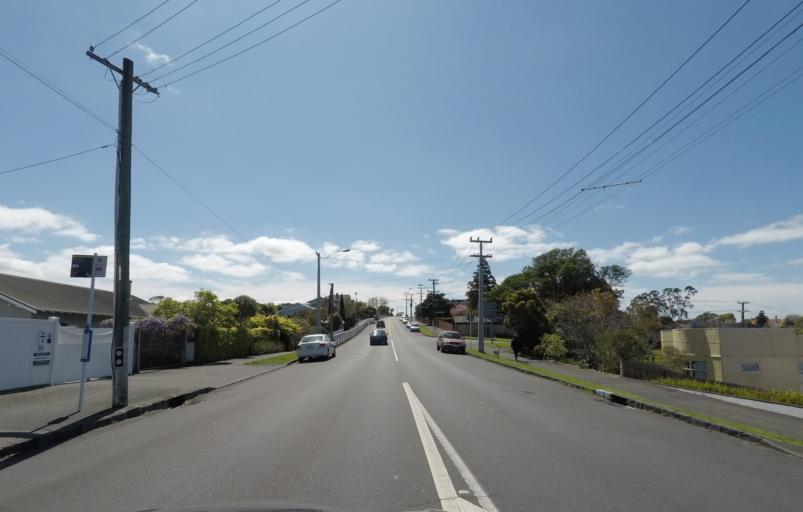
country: NZ
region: Auckland
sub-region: Auckland
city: Auckland
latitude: -36.8860
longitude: 174.8093
